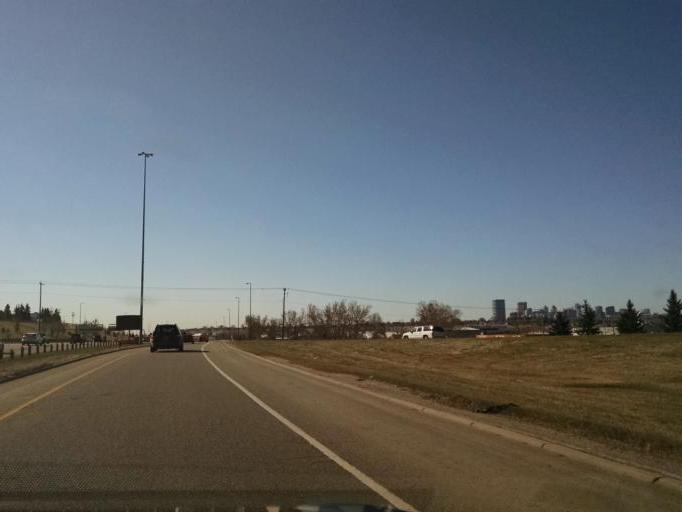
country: CA
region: Alberta
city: Calgary
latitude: 51.0948
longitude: -114.0406
